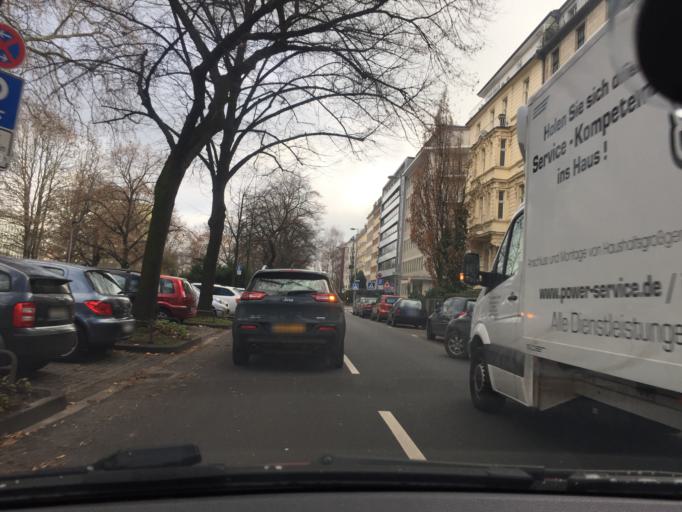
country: DE
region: North Rhine-Westphalia
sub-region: Regierungsbezirk Koln
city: Altstadt Nord
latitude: 50.9501
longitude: 6.9615
